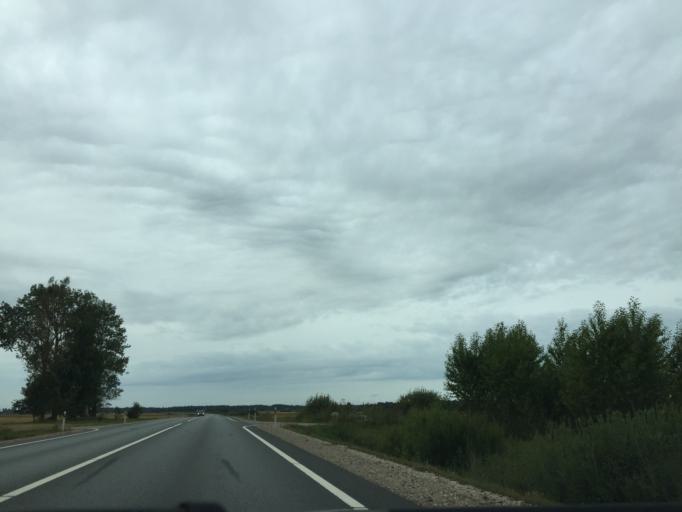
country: LV
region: Dobeles Rajons
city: Dobele
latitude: 56.7369
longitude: 23.2301
